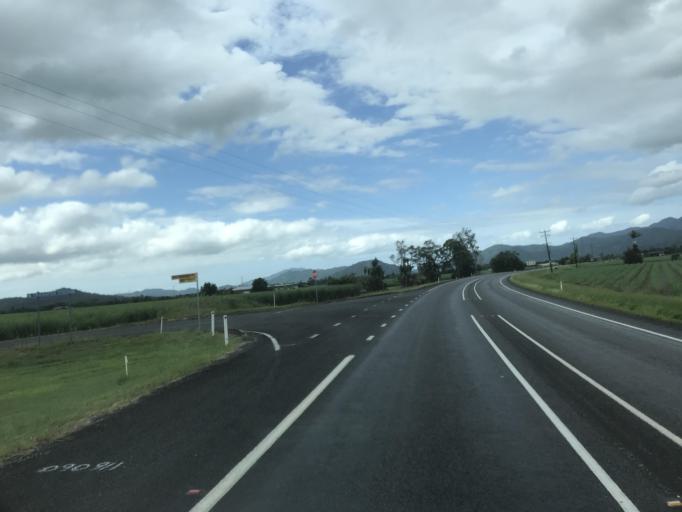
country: AU
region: Queensland
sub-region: Cassowary Coast
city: Innisfail
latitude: -17.7815
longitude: 146.0275
